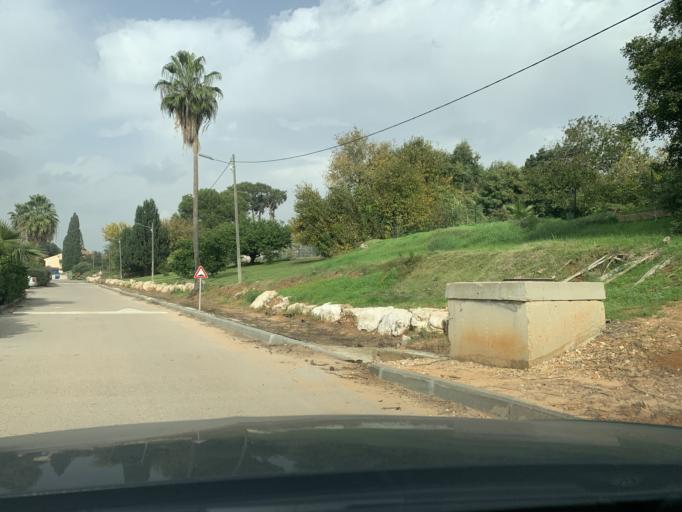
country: IL
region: Central District
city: Tirah
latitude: 32.2144
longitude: 34.9370
